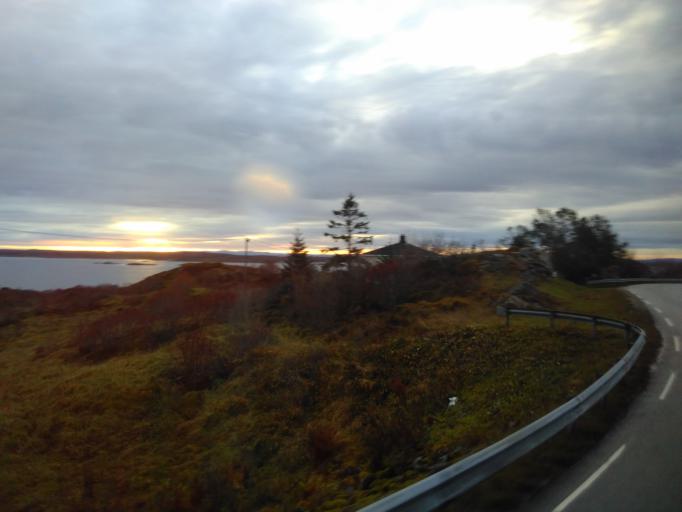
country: NO
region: Sor-Trondelag
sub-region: Froya
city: Sistranda
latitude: 63.7439
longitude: 8.8358
